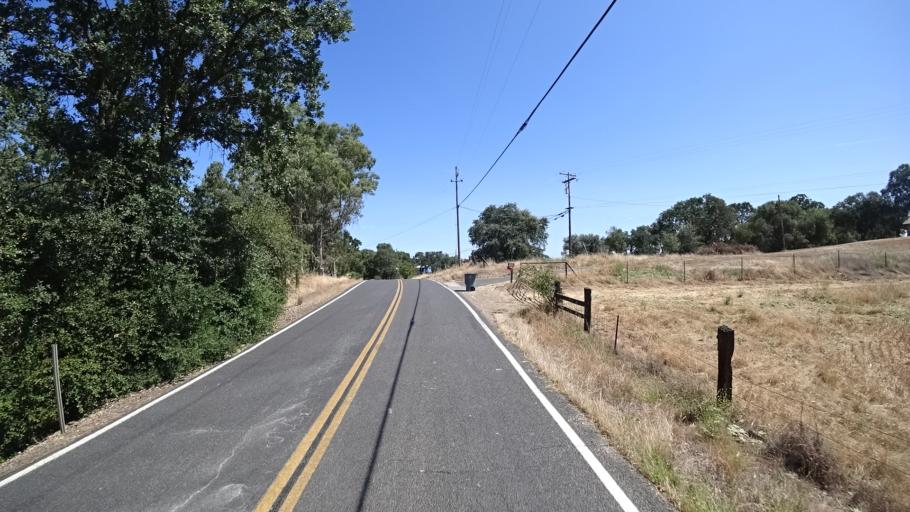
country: US
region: California
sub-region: Calaveras County
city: Rancho Calaveras
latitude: 38.1732
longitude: -120.9575
